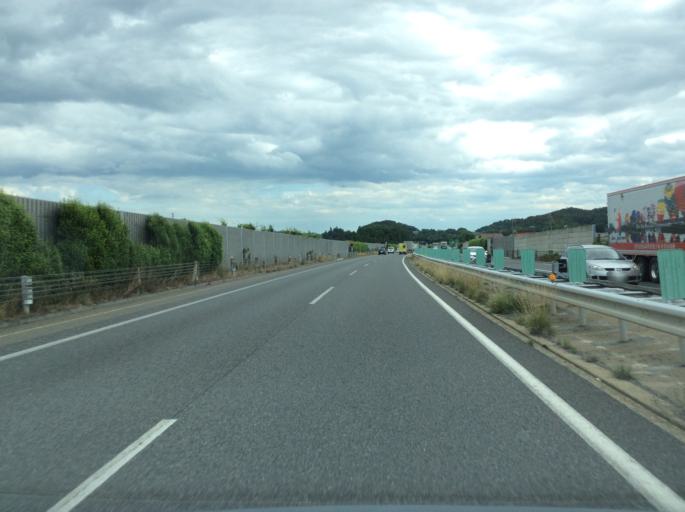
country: JP
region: Fukushima
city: Motomiya
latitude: 37.5254
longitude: 140.3830
